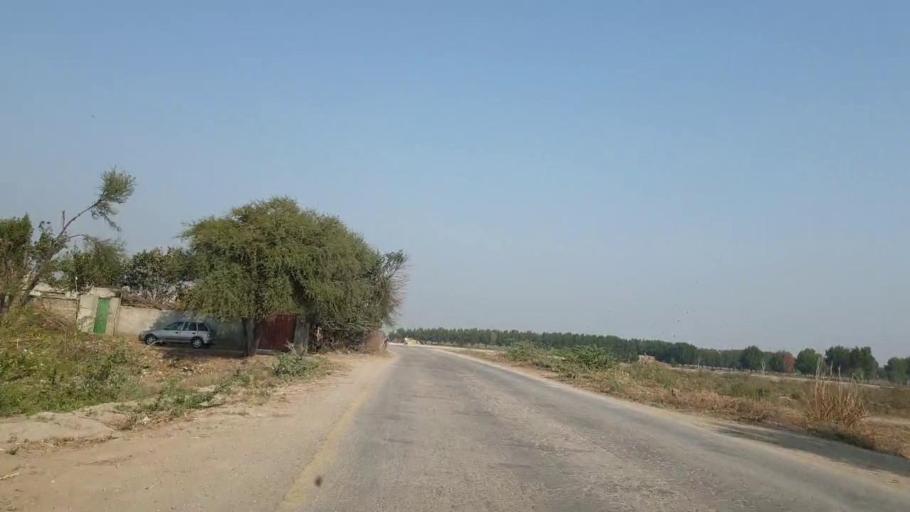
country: PK
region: Sindh
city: Mirpur Khas
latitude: 25.5383
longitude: 69.0448
